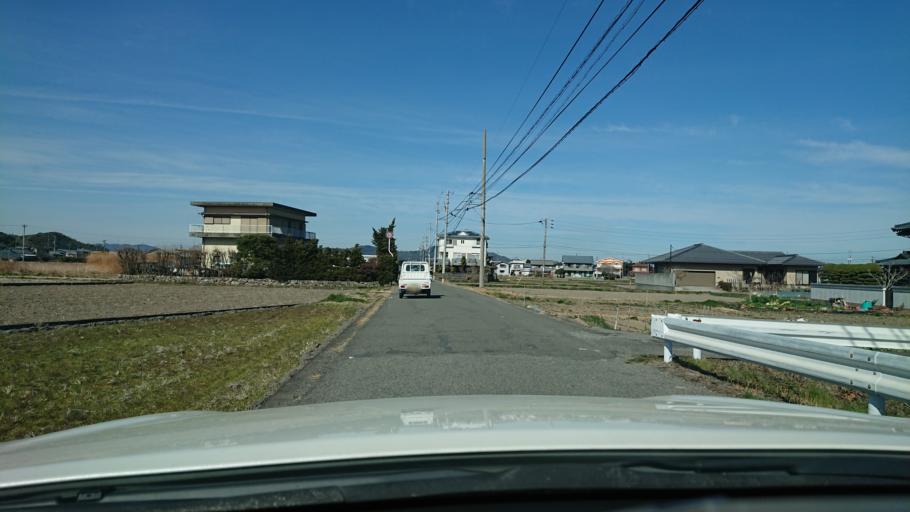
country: JP
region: Tokushima
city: Komatsushimacho
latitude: 33.9808
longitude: 134.5883
